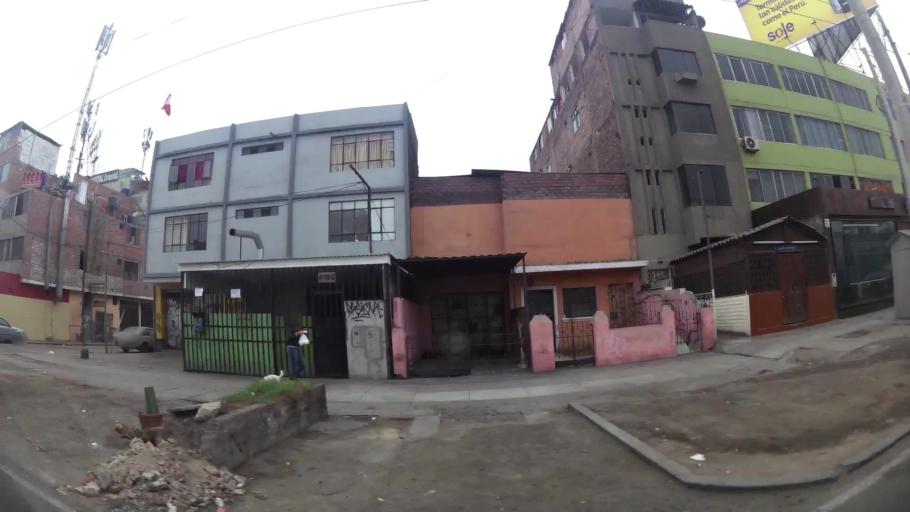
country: PE
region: Lima
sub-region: Lima
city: San Isidro
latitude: -12.1067
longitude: -77.0187
